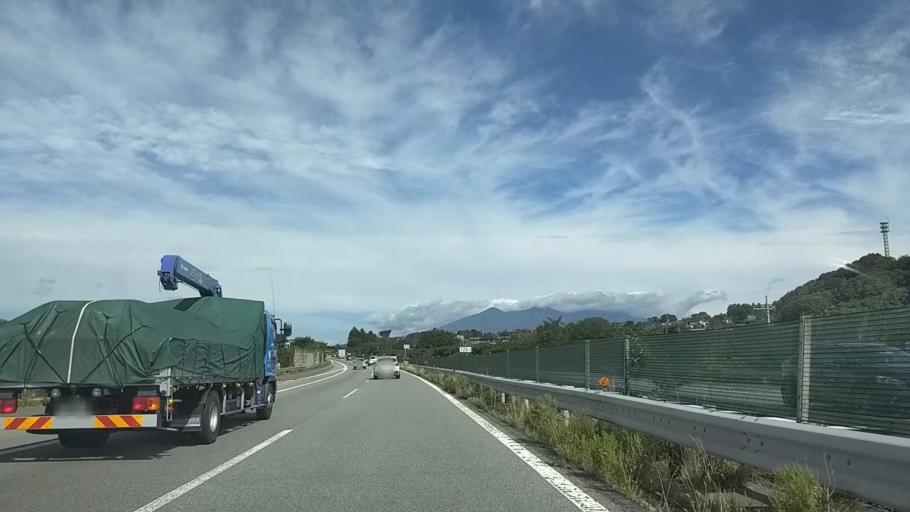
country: JP
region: Yamanashi
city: Nirasaki
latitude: 35.7534
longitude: 138.4406
